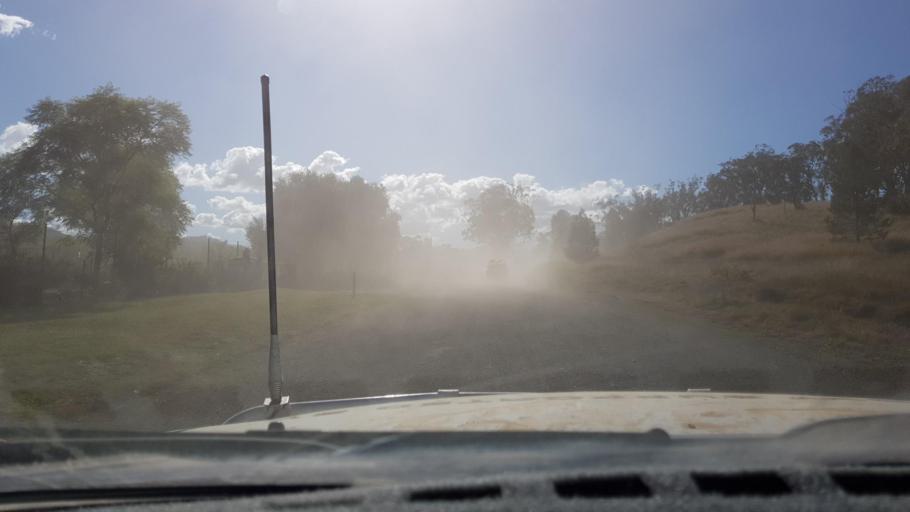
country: AU
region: New South Wales
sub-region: Narrabri
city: Blair Athol
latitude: -30.6643
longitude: 150.4648
